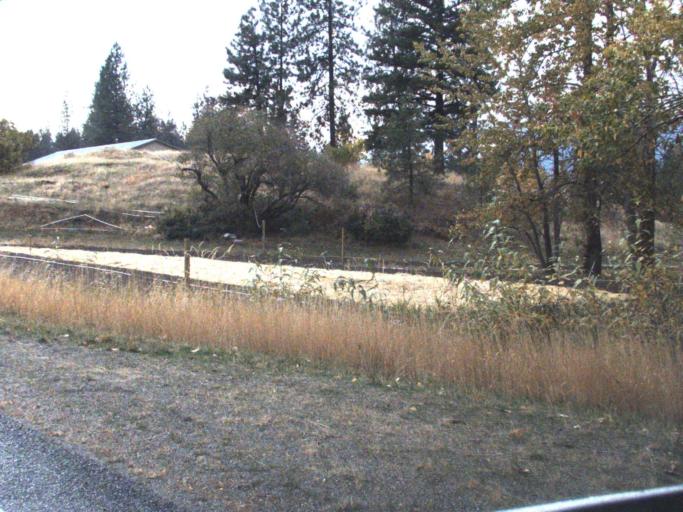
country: US
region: Washington
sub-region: Stevens County
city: Kettle Falls
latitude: 48.5566
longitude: -118.1228
